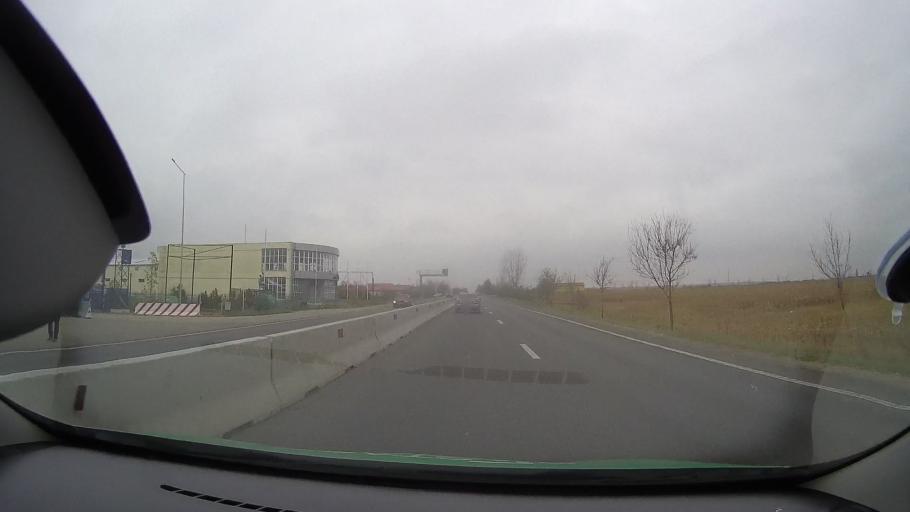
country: RO
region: Ilfov
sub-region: Comuna Balotesti
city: Balotesti
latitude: 44.6642
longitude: 26.0763
